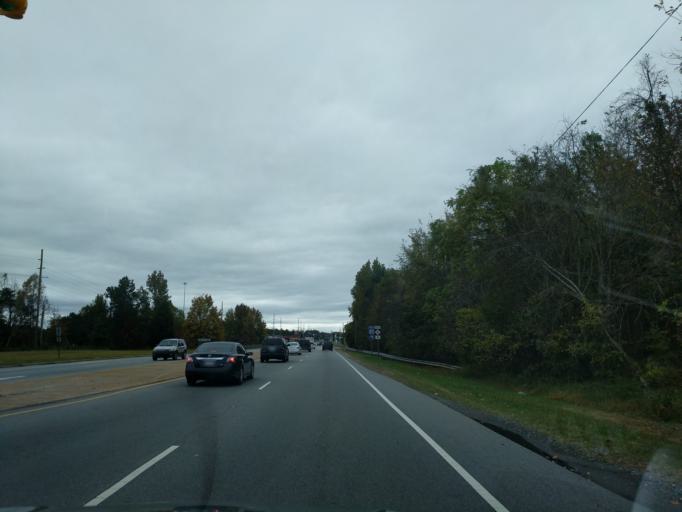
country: US
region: North Carolina
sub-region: Davidson County
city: Lexington
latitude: 35.7821
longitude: -80.2603
